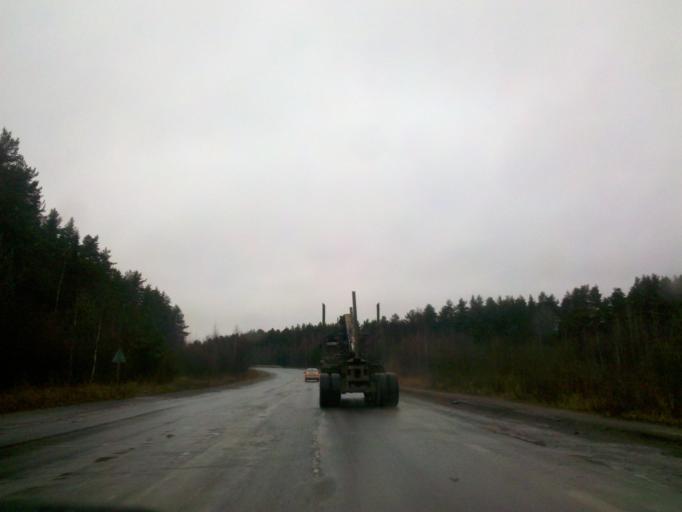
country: RU
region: Republic of Karelia
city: Shuya
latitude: 61.8552
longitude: 34.1793
